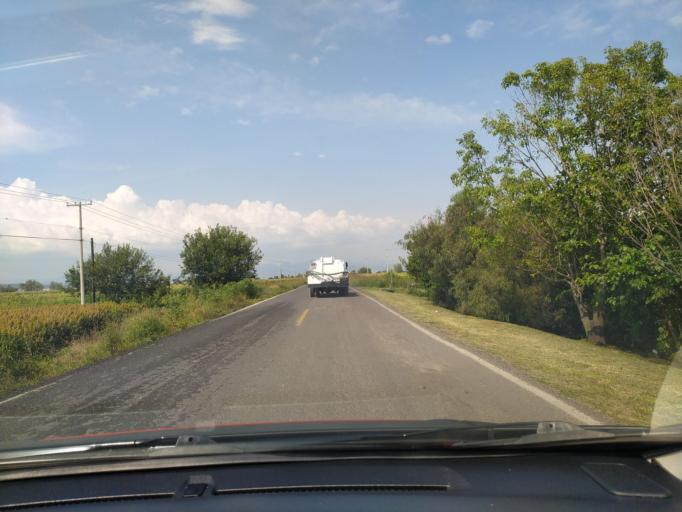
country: MX
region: Guanajuato
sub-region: Leon
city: Malagana (San Antonio del Monte)
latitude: 21.0526
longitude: -101.7484
